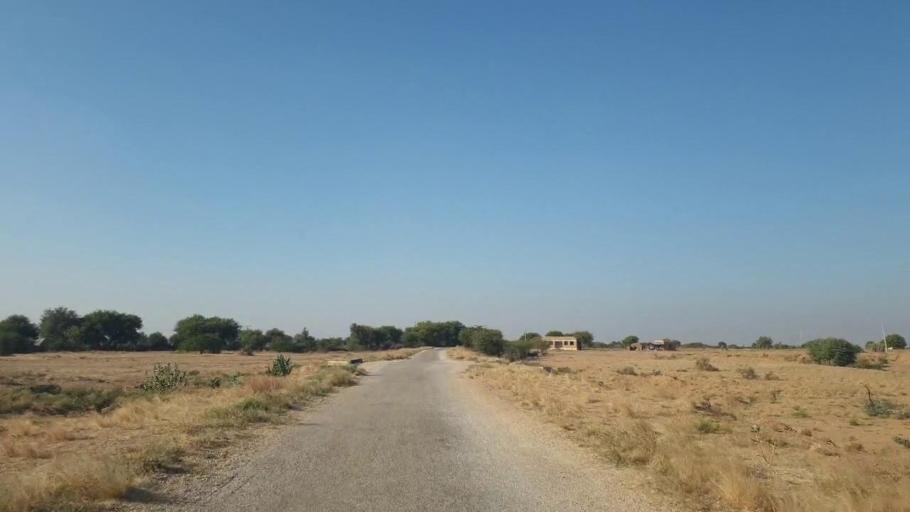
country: PK
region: Sindh
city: Malir Cantonment
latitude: 25.4194
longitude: 67.4630
